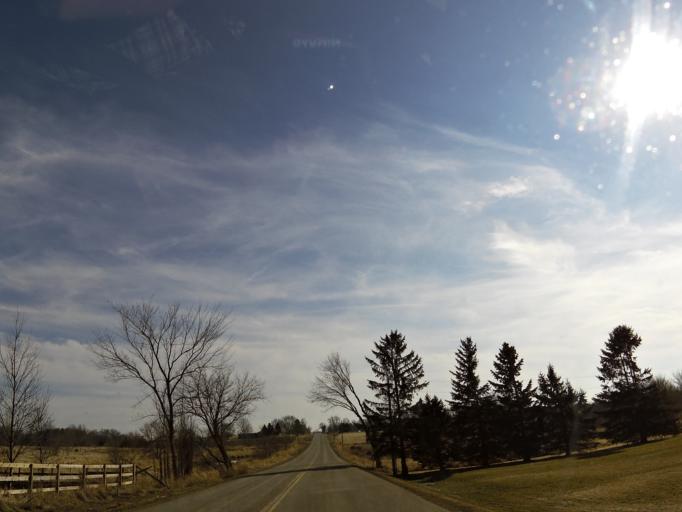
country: US
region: Minnesota
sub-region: Scott County
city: Prior Lake
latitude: 44.6785
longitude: -93.4806
